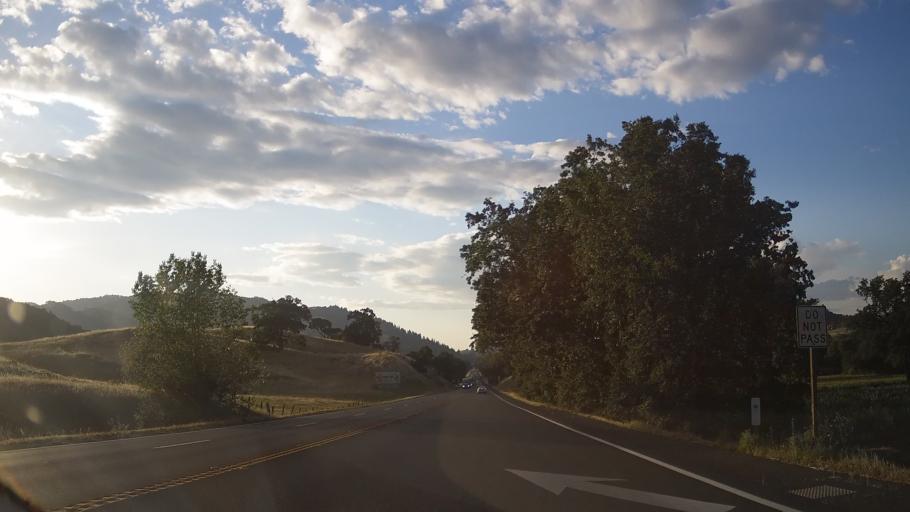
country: US
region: California
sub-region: Mendocino County
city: Talmage
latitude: 39.0324
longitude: -123.1421
